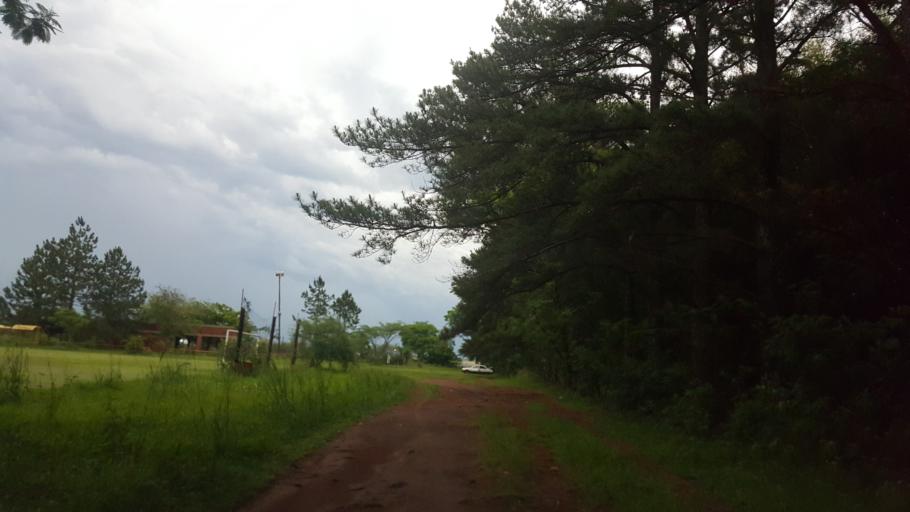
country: AR
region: Misiones
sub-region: Departamento de Capital
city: Posadas
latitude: -27.4003
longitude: -55.9734
